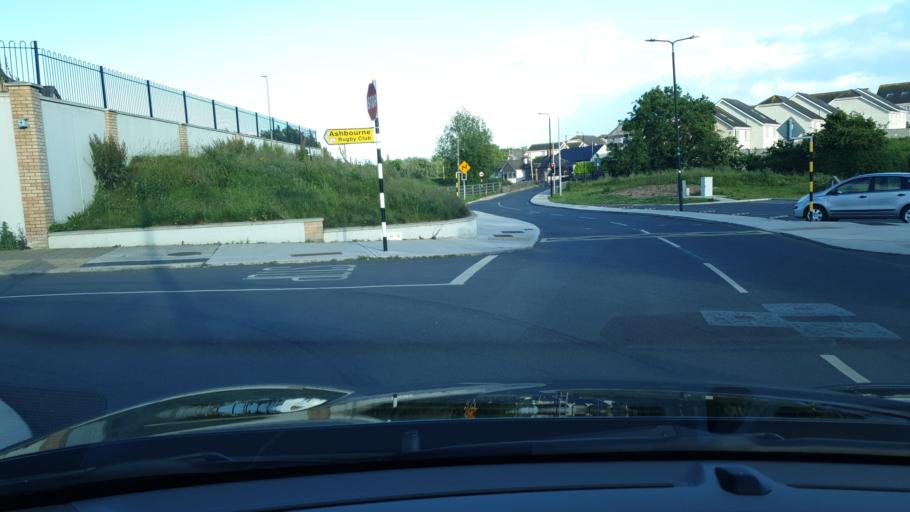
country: IE
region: Leinster
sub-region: An Mhi
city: Ashbourne
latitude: 53.5058
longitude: -6.3854
